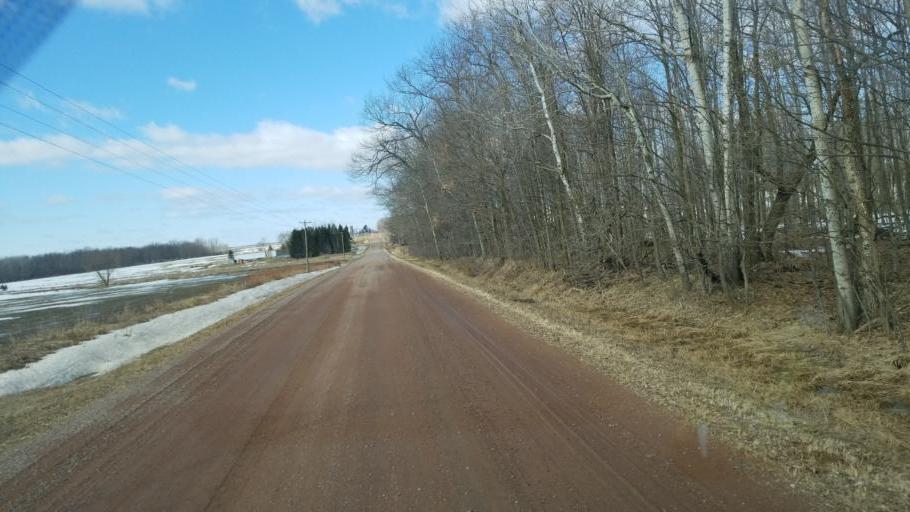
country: US
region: Wisconsin
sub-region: Clark County
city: Loyal
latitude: 44.6835
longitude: -90.4431
